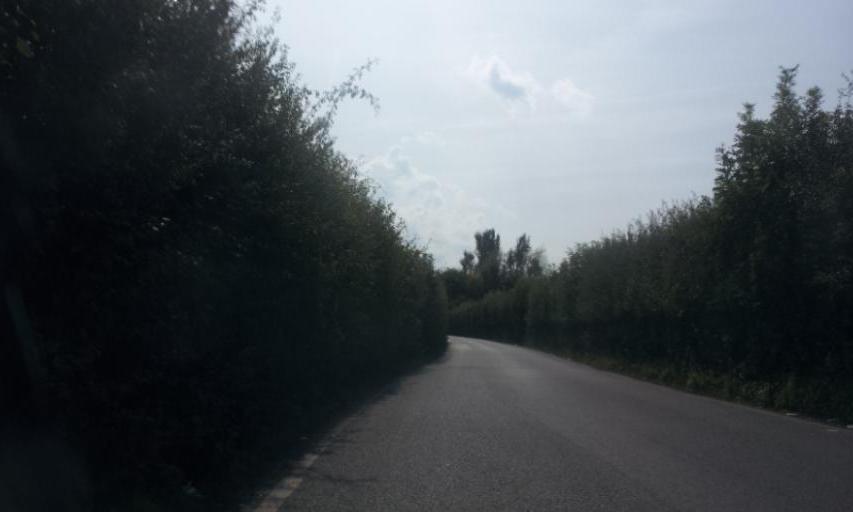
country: GB
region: England
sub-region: Kent
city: Paddock Wood
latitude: 51.1704
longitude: 0.4017
